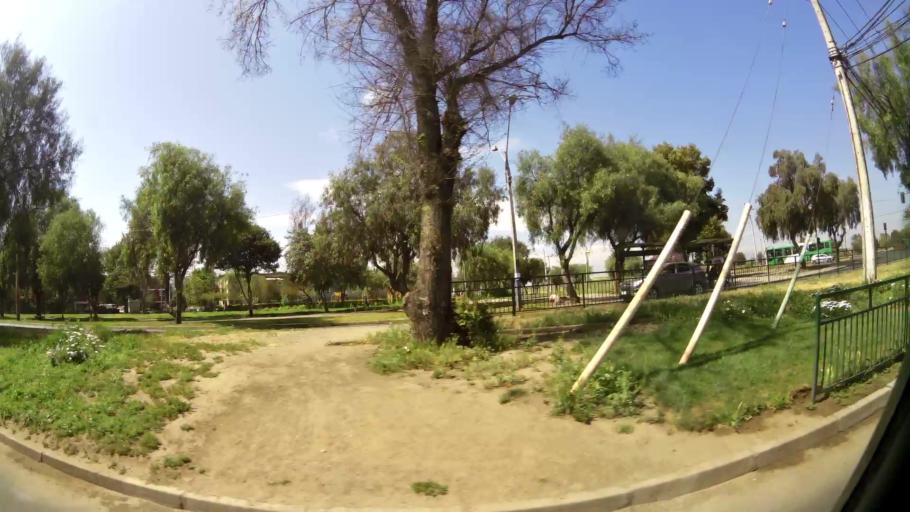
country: CL
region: Santiago Metropolitan
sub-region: Provincia de Santiago
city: Lo Prado
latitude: -33.4814
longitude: -70.7244
